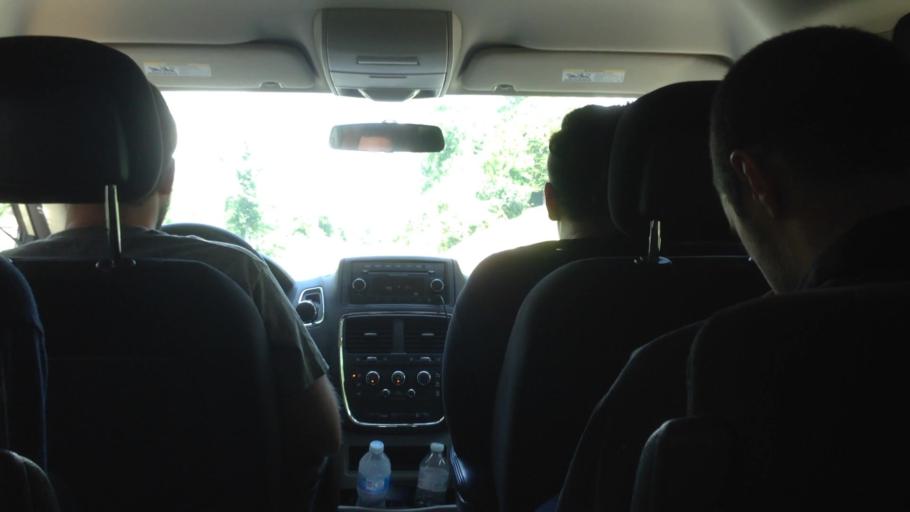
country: US
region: New York
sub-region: Dutchess County
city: Tivoli
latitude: 42.0990
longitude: -73.8961
